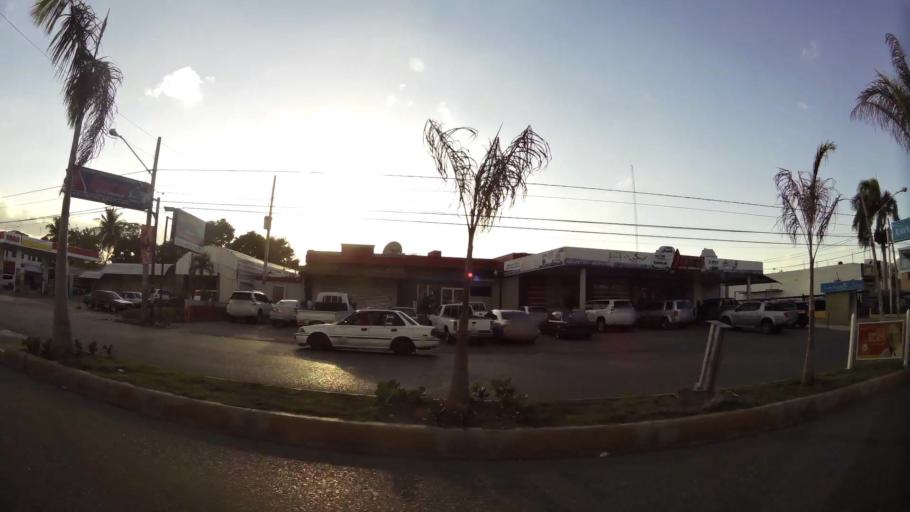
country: DO
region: Santiago
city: Santiago de los Caballeros
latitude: 19.4858
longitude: -70.7189
